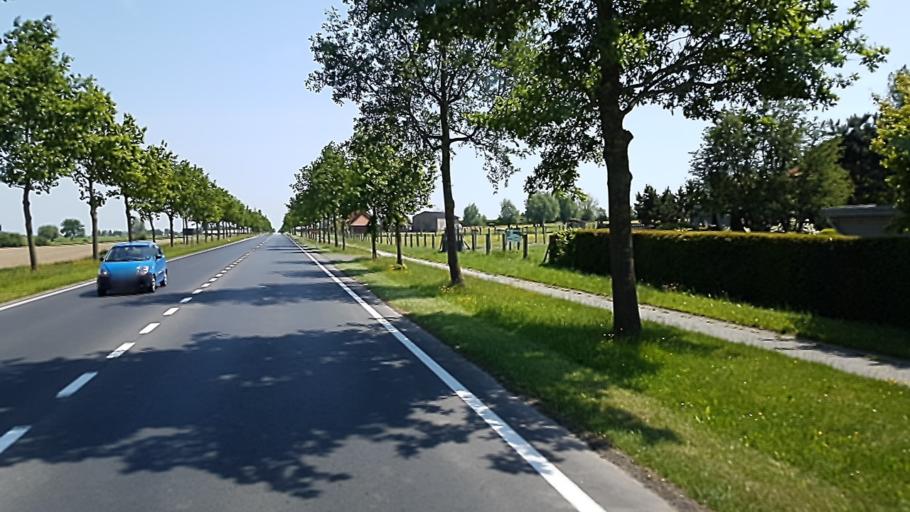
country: BE
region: Flanders
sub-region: Provincie West-Vlaanderen
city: Wervik
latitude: 50.8264
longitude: 3.0189
